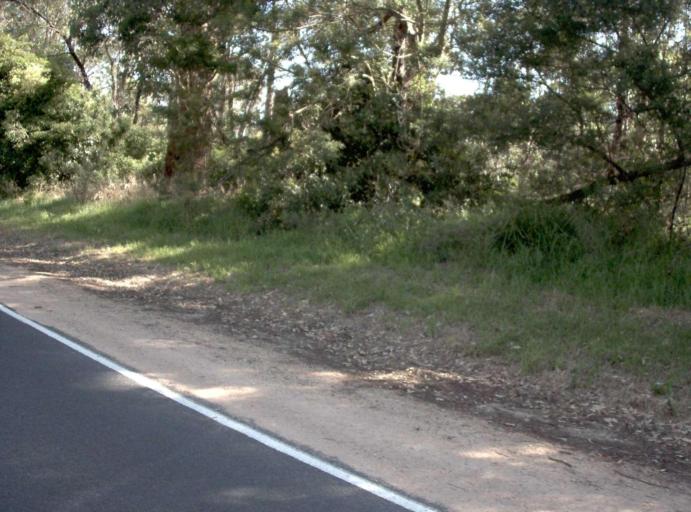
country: AU
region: Victoria
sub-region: East Gippsland
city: Lakes Entrance
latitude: -37.7155
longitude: 148.4556
